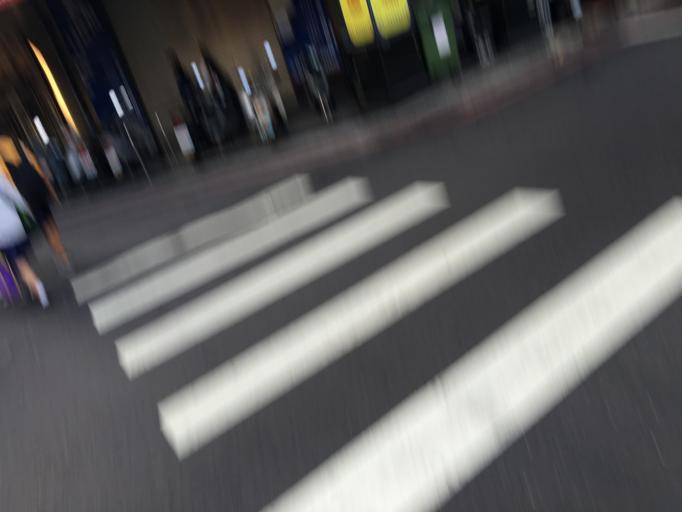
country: TW
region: Taiwan
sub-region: Taichung City
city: Taichung
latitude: 24.1351
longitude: 120.6849
